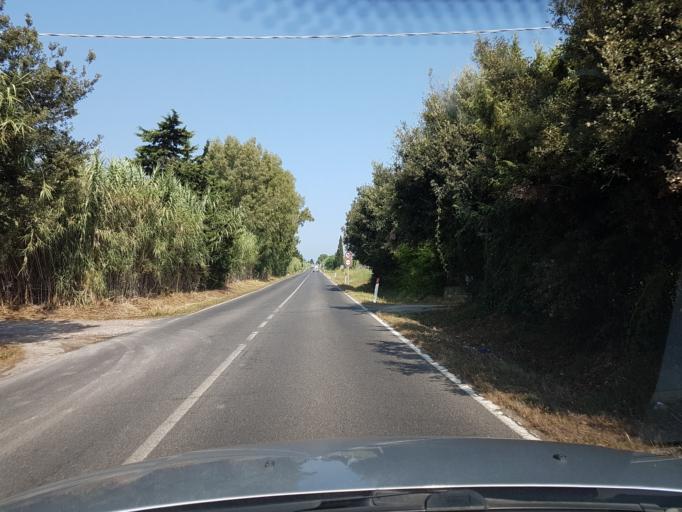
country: IT
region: Sardinia
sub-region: Provincia di Oristano
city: Donigala Fenugheddu
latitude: 39.9456
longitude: 8.5668
